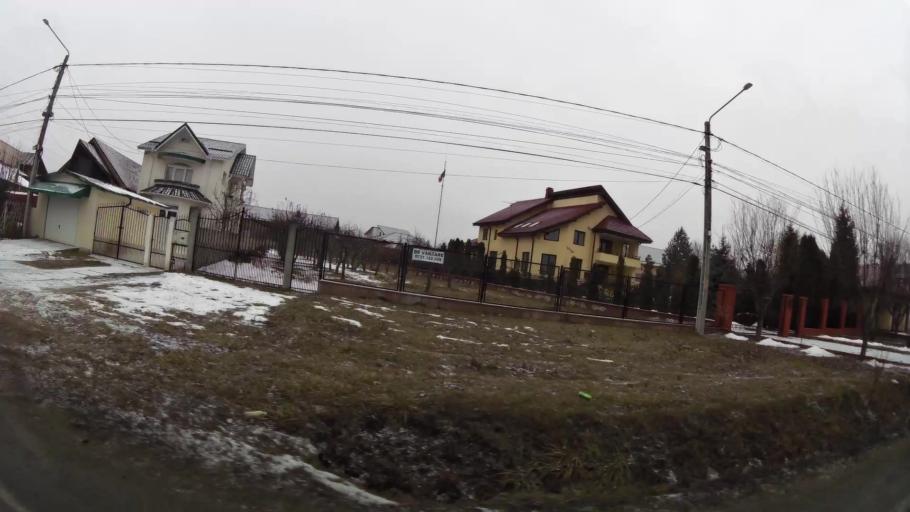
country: RO
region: Dambovita
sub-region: Comuna Aninoasa
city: Viforata
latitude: 44.9512
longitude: 25.4763
